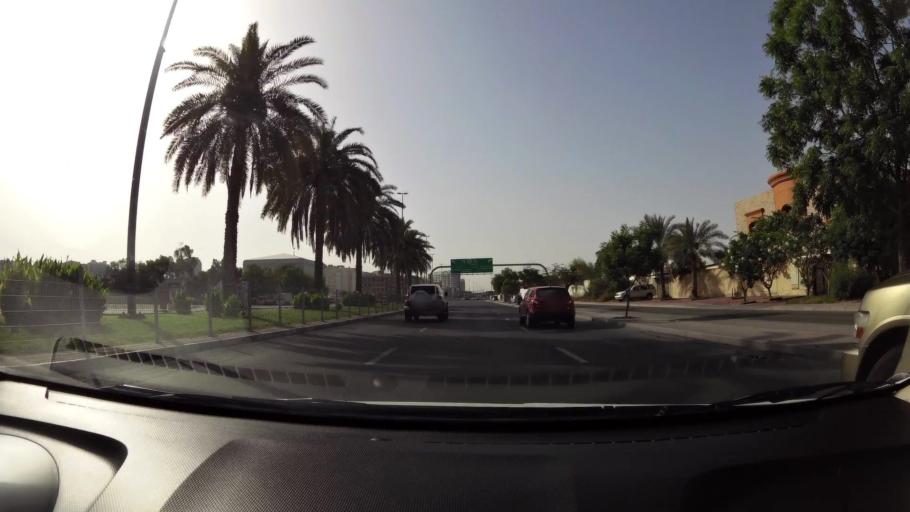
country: AE
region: Ash Shariqah
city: Sharjah
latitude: 25.2878
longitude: 55.3482
